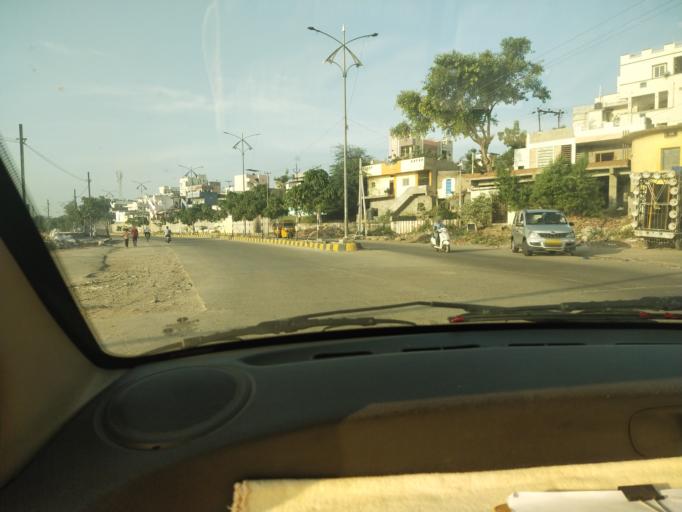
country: IN
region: Telangana
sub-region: Hyderabad
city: Hyderabad
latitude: 17.3671
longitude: 78.4565
